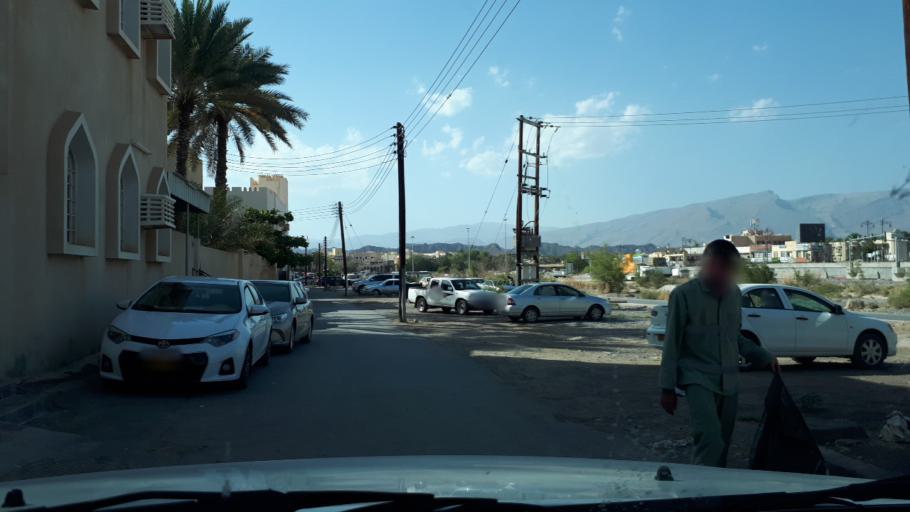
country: OM
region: Muhafazat ad Dakhiliyah
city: Nizwa
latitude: 22.9296
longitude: 57.5340
